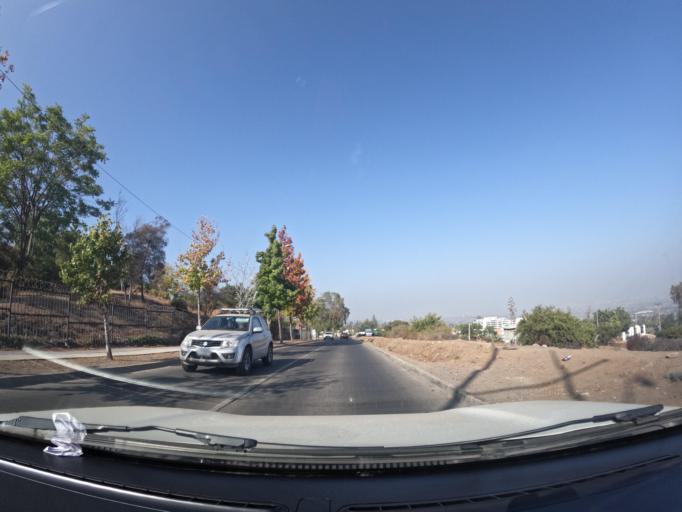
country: CL
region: Santiago Metropolitan
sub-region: Provincia de Santiago
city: Villa Presidente Frei, Nunoa, Santiago, Chile
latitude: -33.4637
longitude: -70.5218
